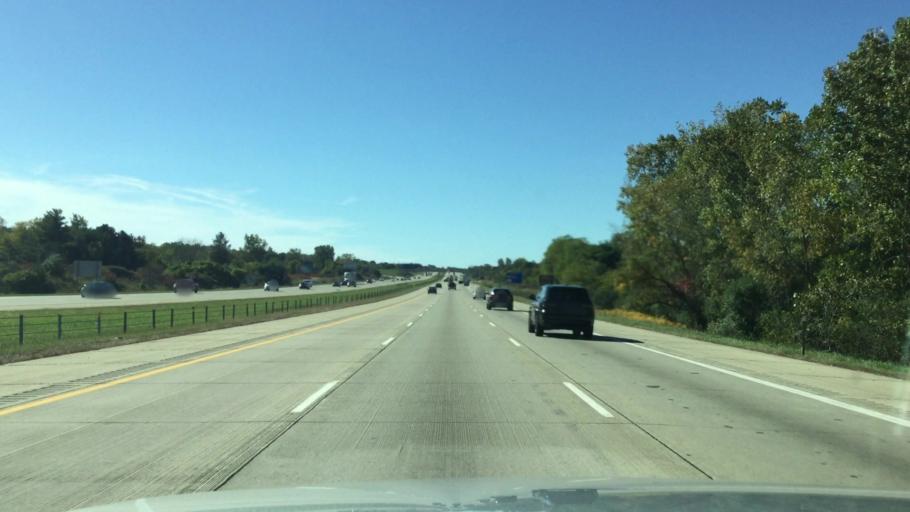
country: US
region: Michigan
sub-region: Wayne County
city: Plymouth
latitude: 42.3830
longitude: -83.4948
